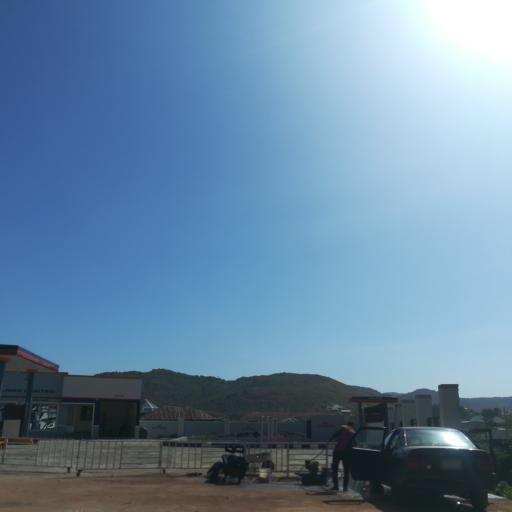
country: NG
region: Plateau
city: Jos
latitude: 9.9410
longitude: 8.9075
